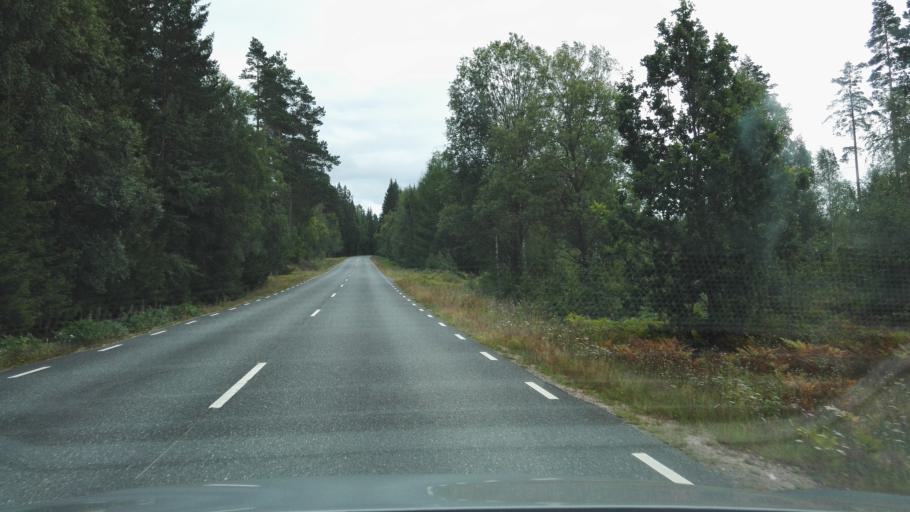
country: SE
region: Joenkoeping
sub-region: Vetlanda Kommun
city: Landsbro
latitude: 57.2534
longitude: 14.9420
